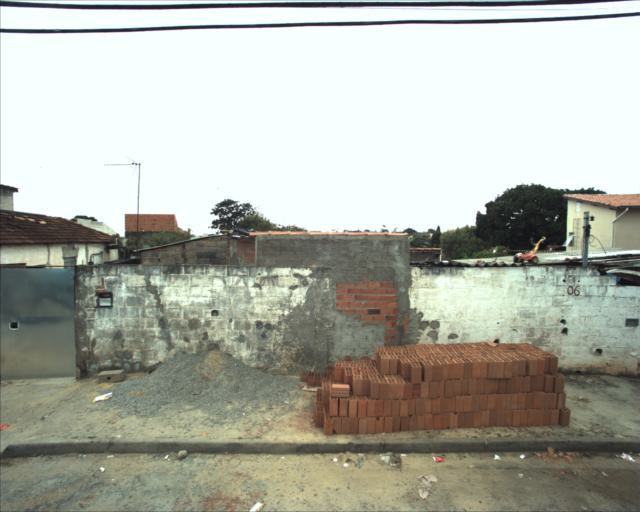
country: BR
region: Sao Paulo
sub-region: Sorocaba
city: Sorocaba
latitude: -23.4795
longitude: -47.4782
